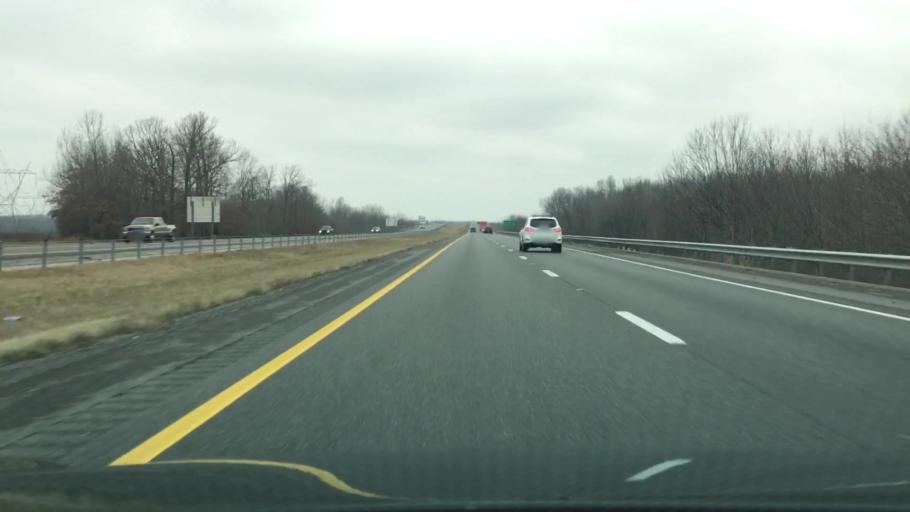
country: US
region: Kentucky
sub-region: McCracken County
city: Hendron
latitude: 37.0207
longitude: -88.6042
